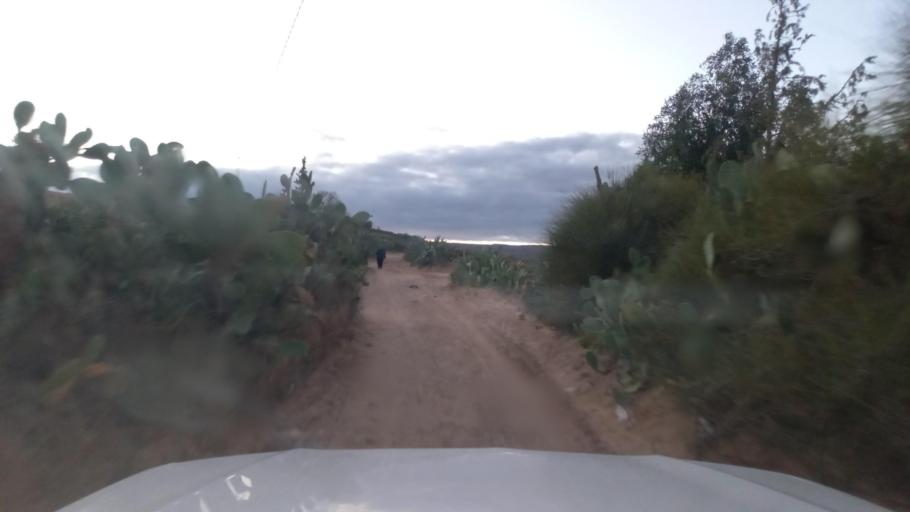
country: TN
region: Al Qasrayn
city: Kasserine
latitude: 35.2574
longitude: 8.9374
